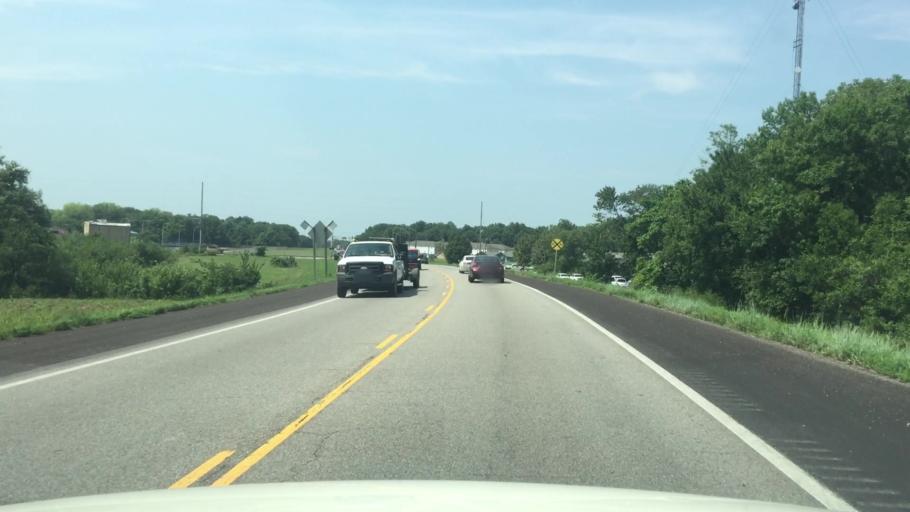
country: US
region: Kansas
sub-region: Crawford County
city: Pittsburg
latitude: 37.3846
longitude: -94.7081
